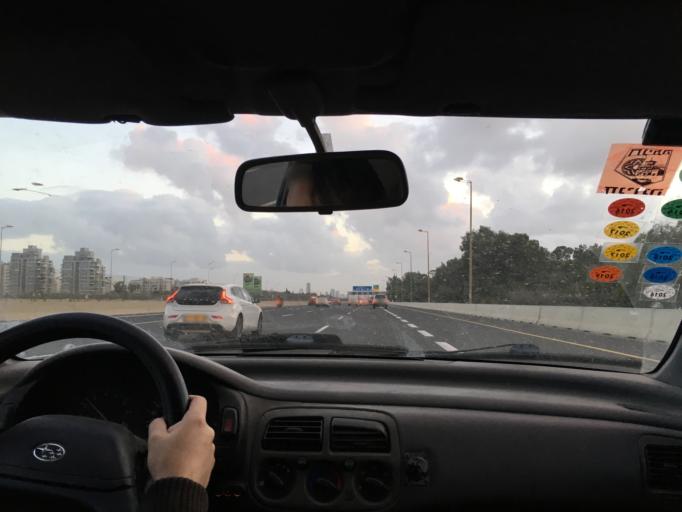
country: IL
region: Tel Aviv
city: Ramat HaSharon
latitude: 32.1299
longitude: 34.8098
